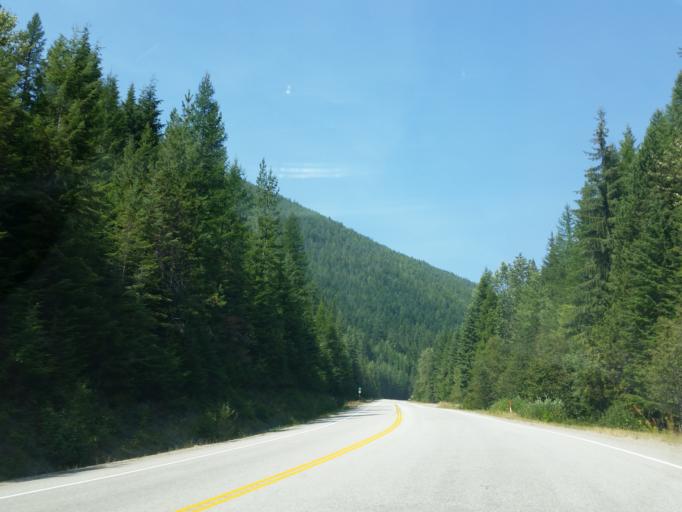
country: CA
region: British Columbia
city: Castlegar
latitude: 49.2782
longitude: -117.7233
